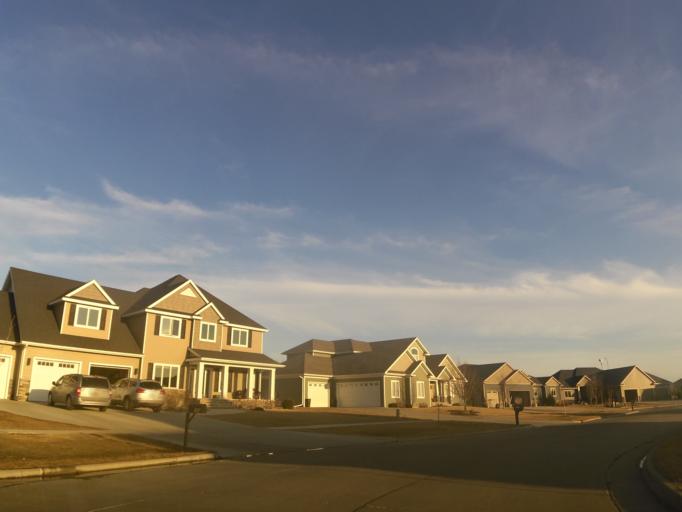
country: US
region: North Dakota
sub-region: Grand Forks County
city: Grand Forks
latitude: 47.8691
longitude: -97.0250
